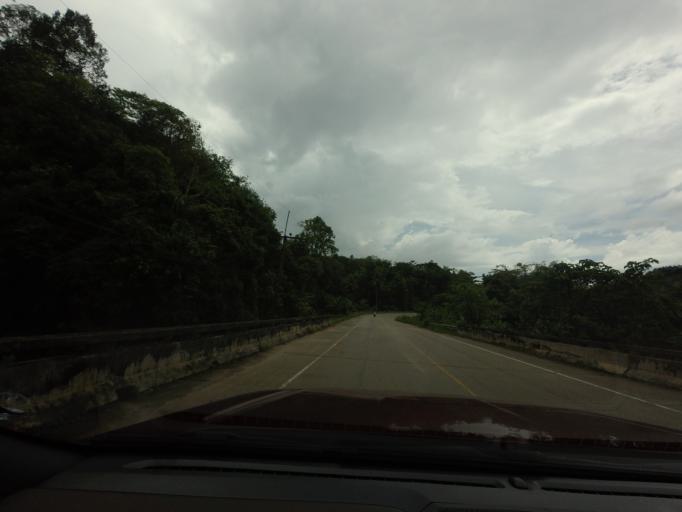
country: TH
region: Narathiwat
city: Sukhirin
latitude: 5.9845
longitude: 101.6877
